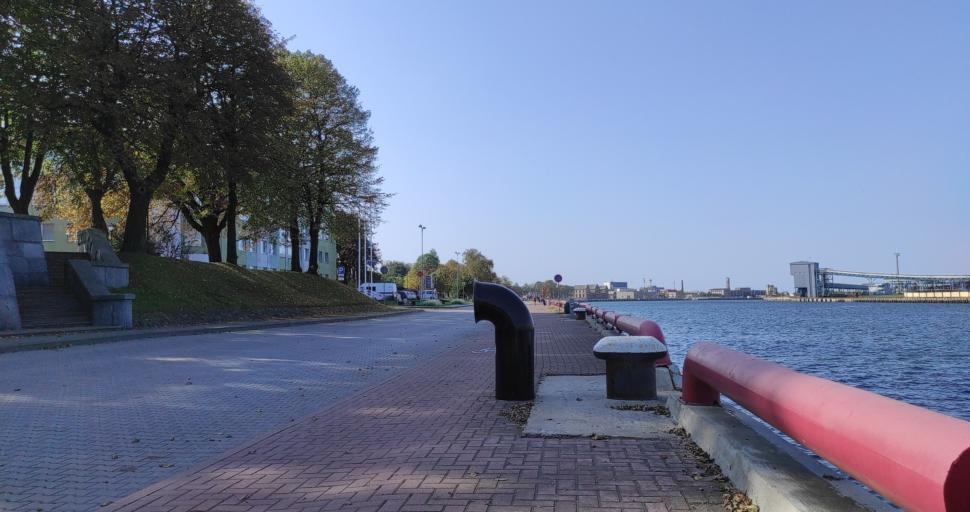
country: LV
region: Ventspils
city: Ventspils
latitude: 57.3965
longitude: 21.5581
